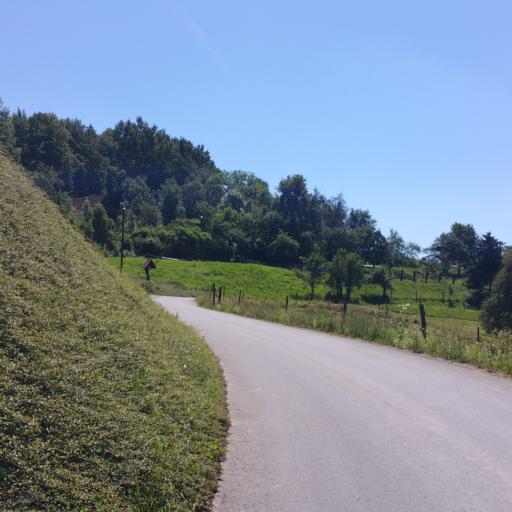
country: AT
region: Styria
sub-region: Politischer Bezirk Leibnitz
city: Gleinstatten
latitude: 46.7346
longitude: 15.3504
